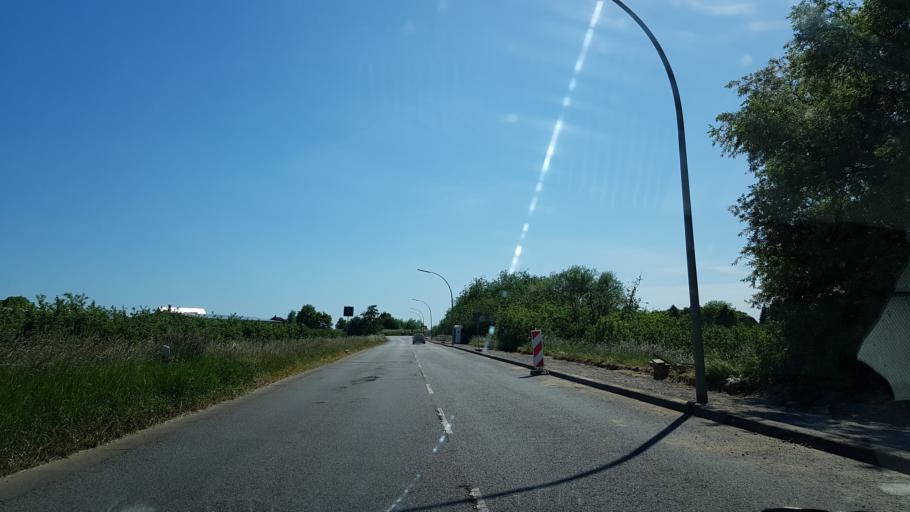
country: DE
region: Lower Saxony
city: Neu Wulmstorf
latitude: 53.5285
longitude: 9.8030
